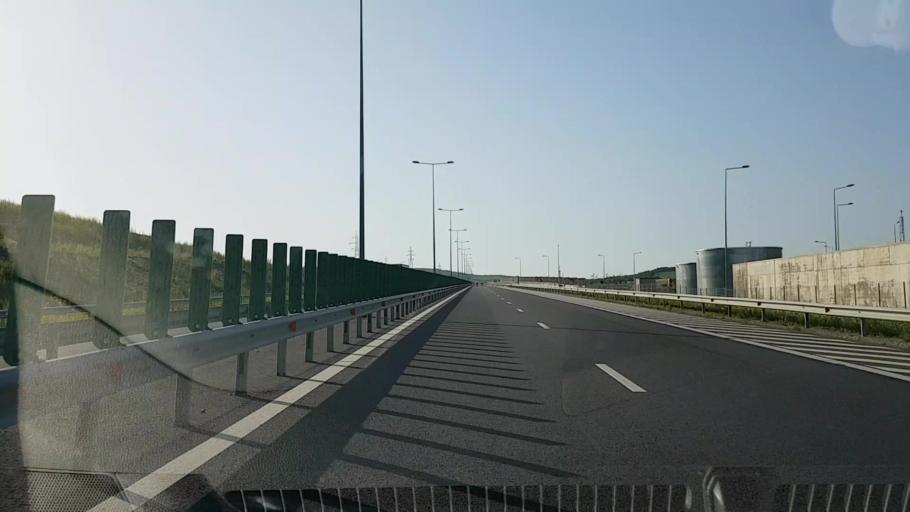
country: RO
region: Alba
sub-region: Comuna Unirea
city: Unirea
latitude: 46.4513
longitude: 23.7929
